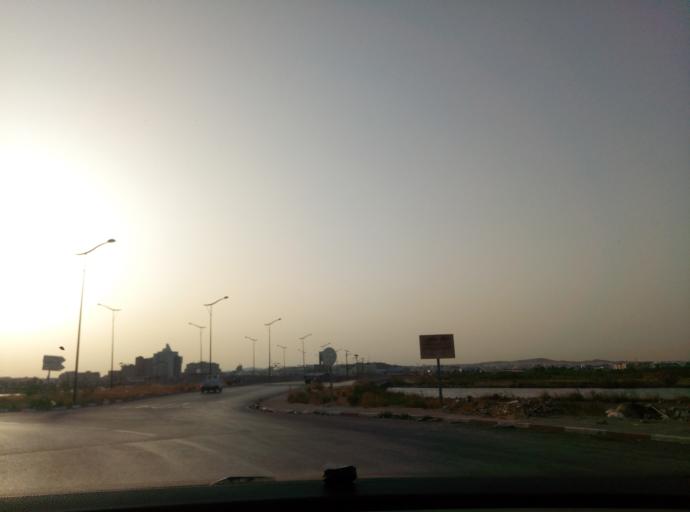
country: TN
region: Tunis
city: Tunis
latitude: 36.8041
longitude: 10.1977
